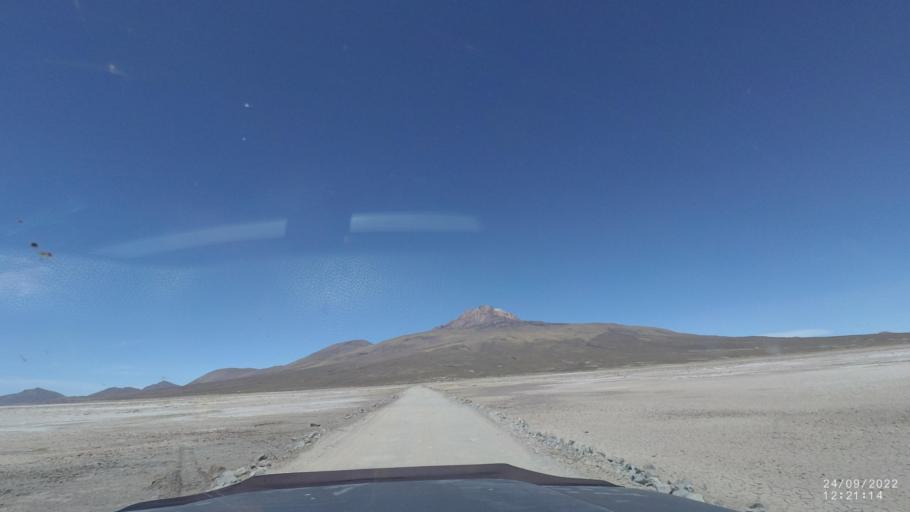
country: BO
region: Potosi
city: Colchani
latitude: -19.7471
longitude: -67.6697
